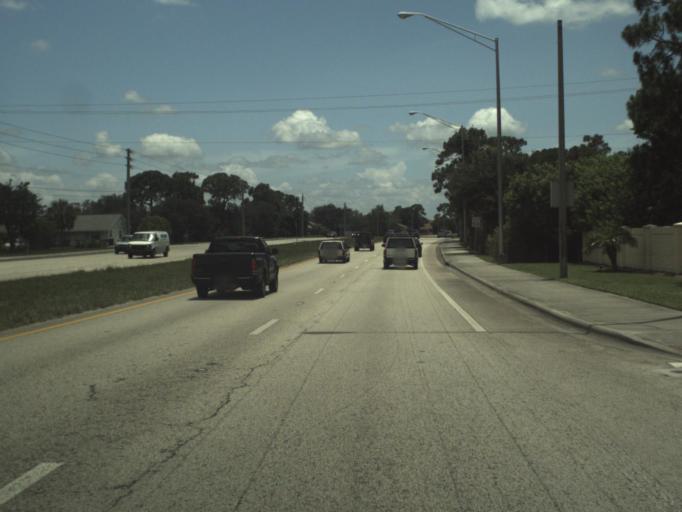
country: US
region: Florida
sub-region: Martin County
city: Palm City
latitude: 27.1518
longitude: -80.2448
